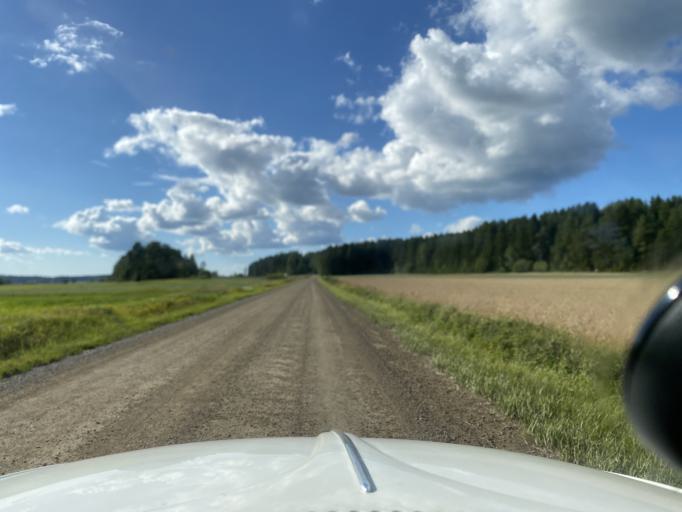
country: FI
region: Pirkanmaa
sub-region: Lounais-Pirkanmaa
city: Punkalaidun
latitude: 61.1362
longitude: 23.2232
